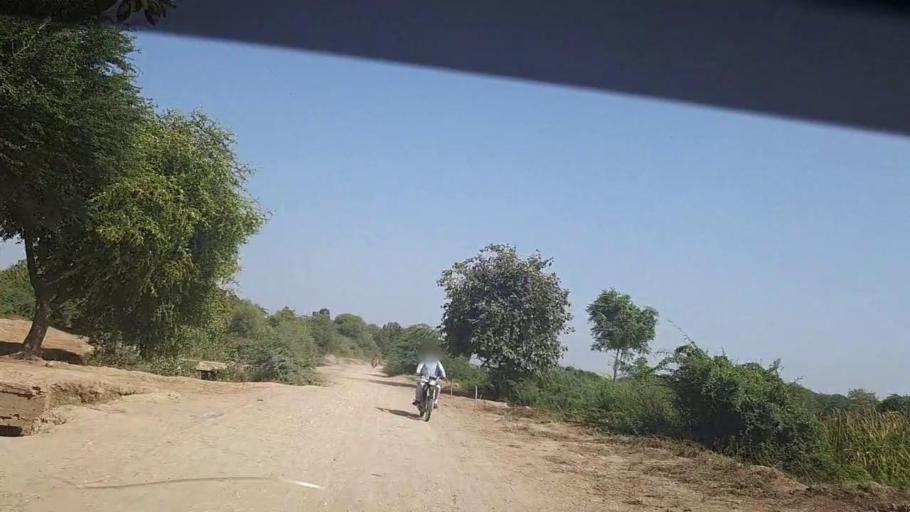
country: PK
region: Sindh
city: Rajo Khanani
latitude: 24.9695
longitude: 68.8759
